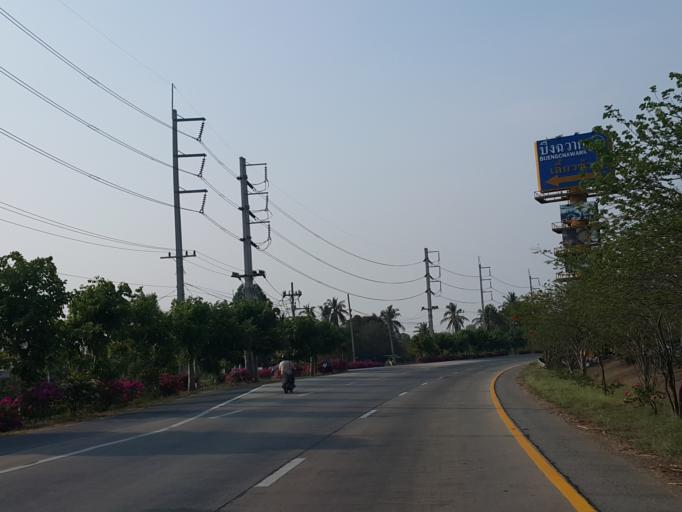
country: TH
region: Suphan Buri
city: Doem Bang Nang Buat
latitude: 14.9105
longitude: 100.0826
